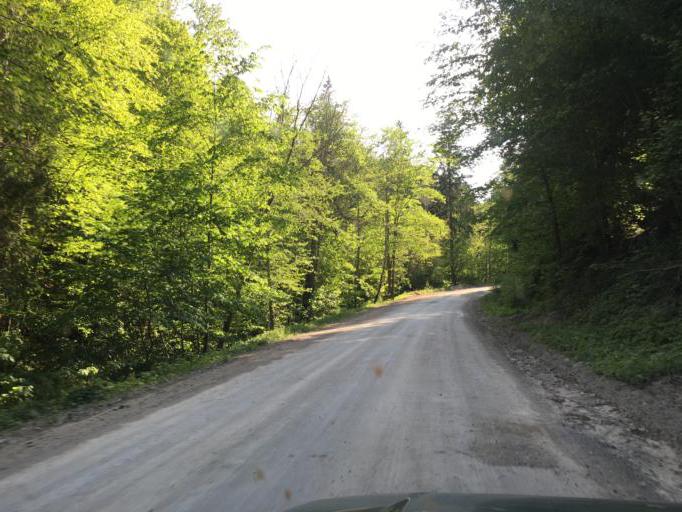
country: LV
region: Dundaga
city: Dundaga
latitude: 57.6079
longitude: 22.4705
